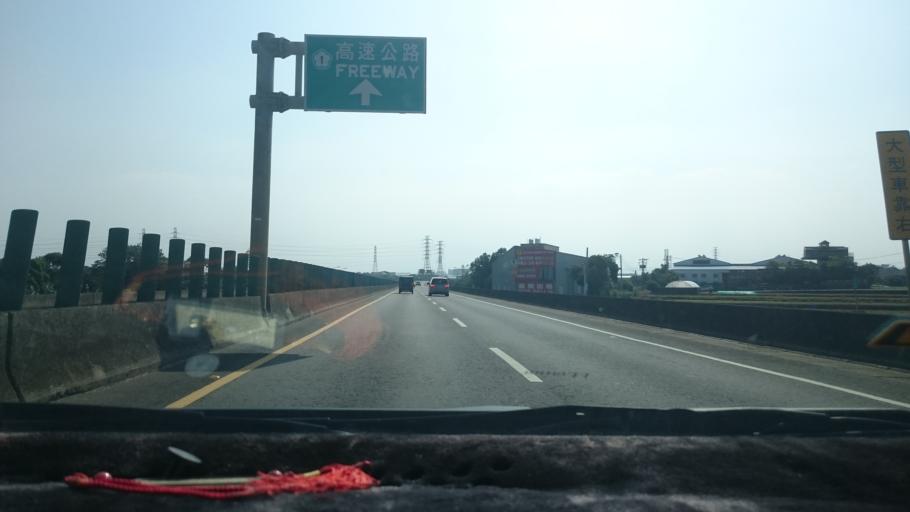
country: TW
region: Taiwan
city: Taoyuan City
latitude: 24.9863
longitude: 121.1253
